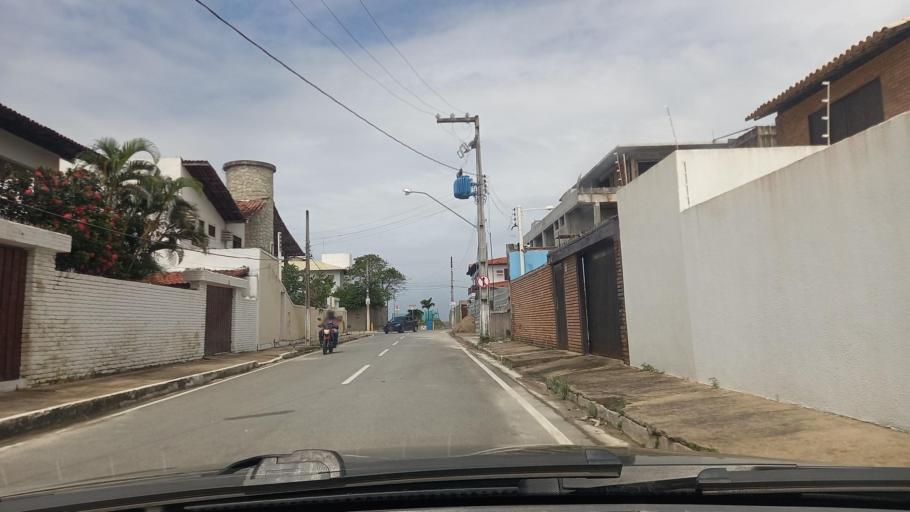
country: BR
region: Alagoas
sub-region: Marechal Deodoro
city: Marechal Deodoro
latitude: -9.8408
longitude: -35.8930
